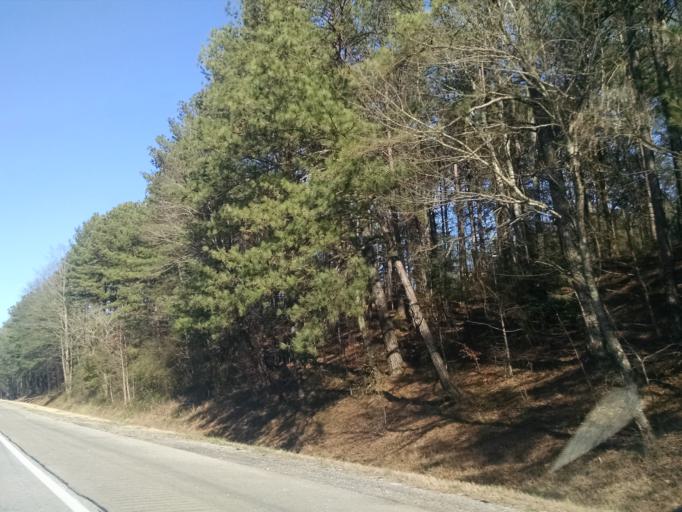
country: US
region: Georgia
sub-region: Gwinnett County
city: Suwanee
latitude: 34.0538
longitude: -84.0250
